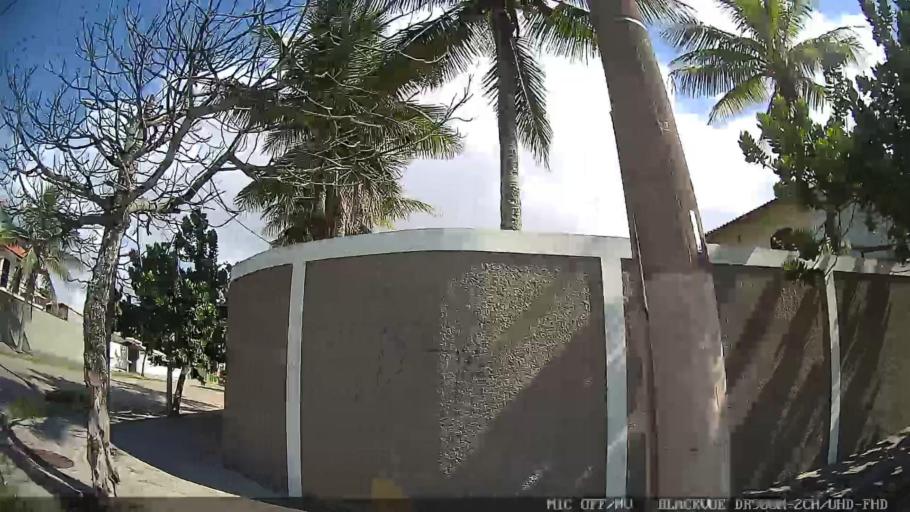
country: BR
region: Sao Paulo
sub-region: Peruibe
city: Peruibe
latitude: -24.2915
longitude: -46.9575
